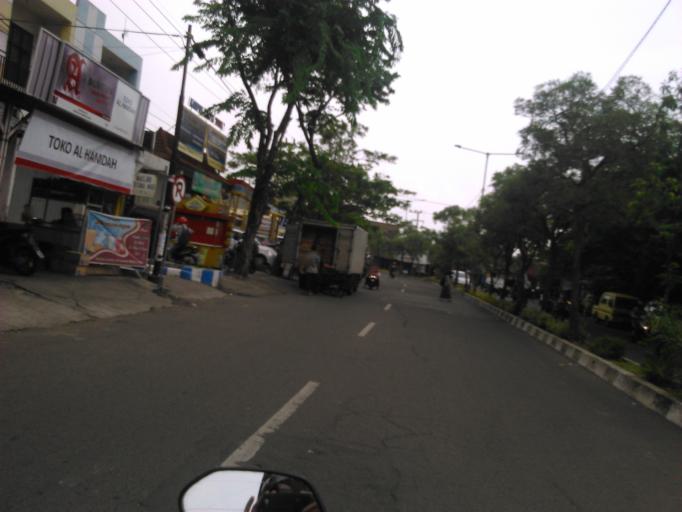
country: ID
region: East Java
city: Gubengairlangga
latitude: -7.2750
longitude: 112.7625
